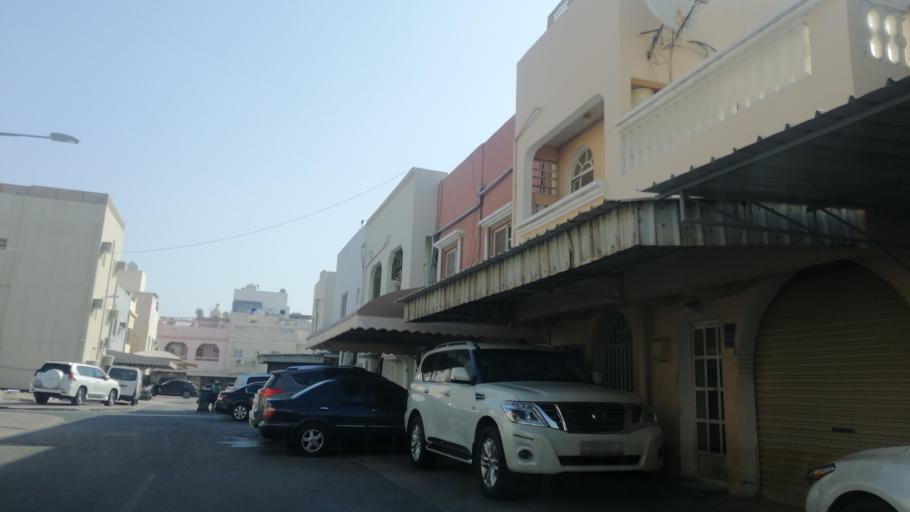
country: BH
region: Muharraq
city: Al Muharraq
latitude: 26.2560
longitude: 50.6325
